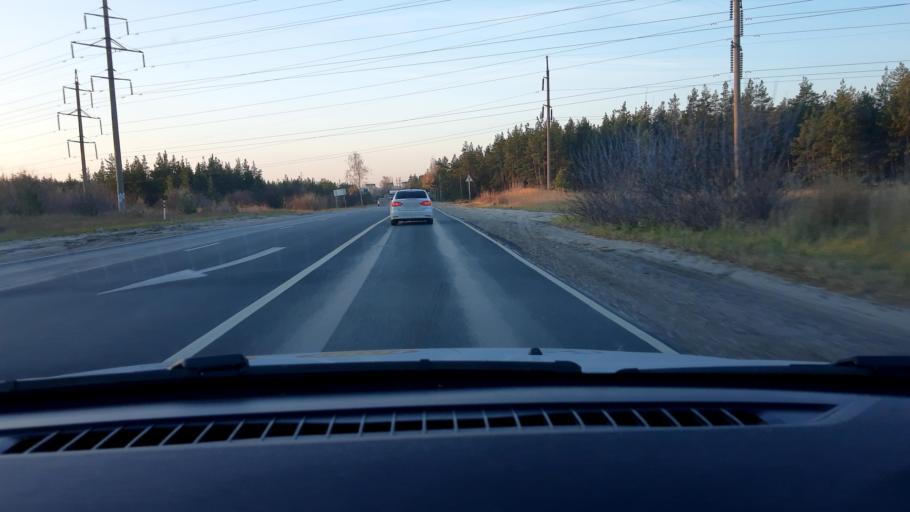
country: RU
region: Nizjnij Novgorod
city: Dzerzhinsk
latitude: 56.2677
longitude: 43.4713
